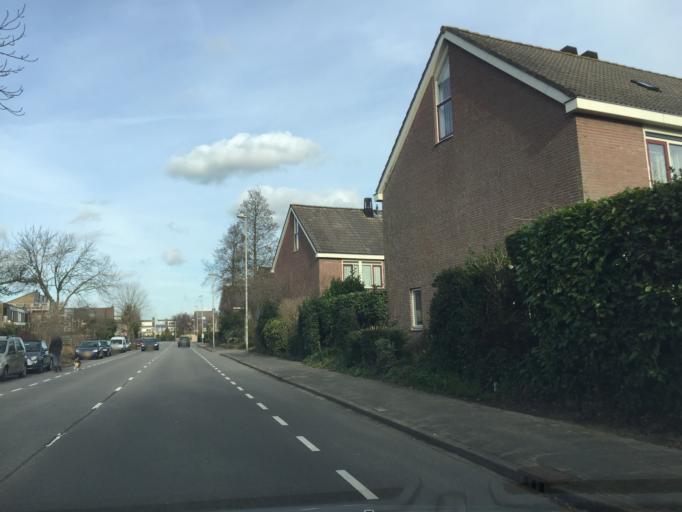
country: NL
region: South Holland
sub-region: Gemeente Leiderdorp
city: Leiderdorp
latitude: 52.1586
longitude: 4.5385
